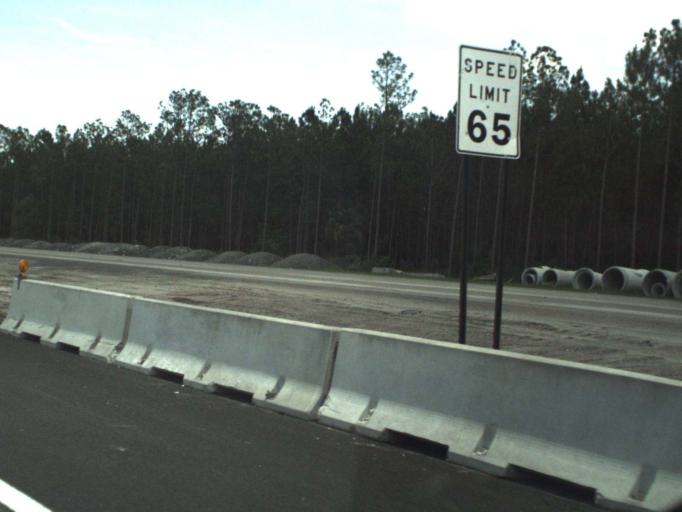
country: US
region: Florida
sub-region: Volusia County
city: South Daytona
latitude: 29.1467
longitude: -81.0964
